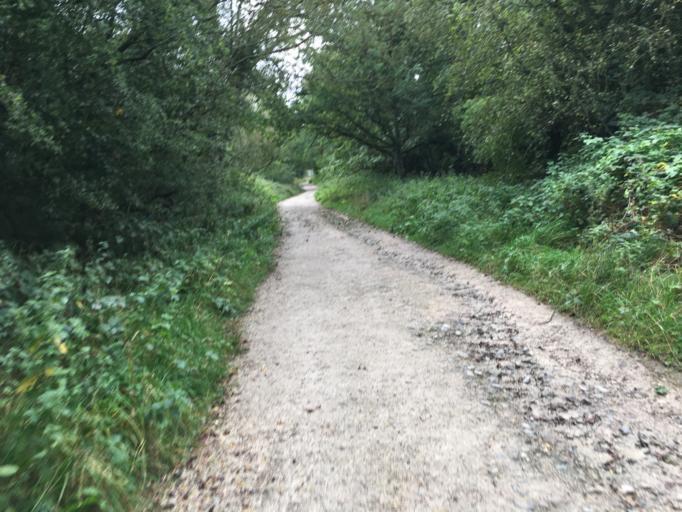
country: GB
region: England
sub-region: North Yorkshire
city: Sleights
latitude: 54.4042
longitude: -0.7249
